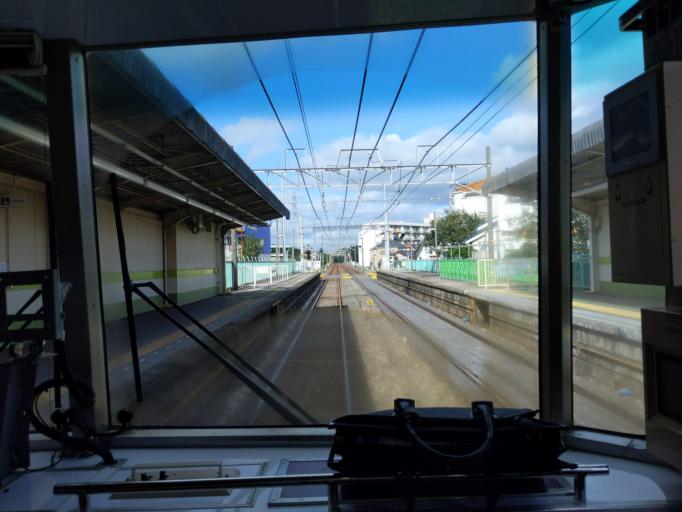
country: JP
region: Chiba
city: Funabashi
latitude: 35.7383
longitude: 140.0265
